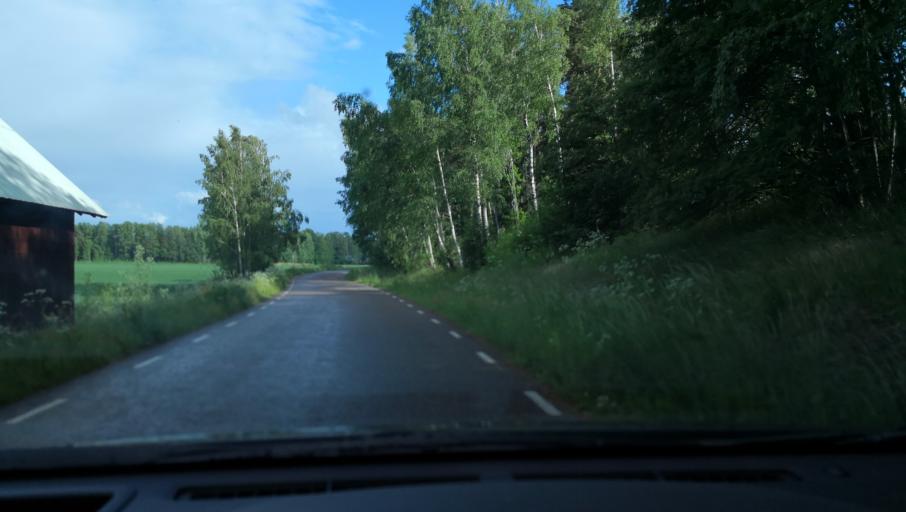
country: SE
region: OErebro
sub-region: Lindesbergs Kommun
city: Fellingsbro
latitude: 59.3094
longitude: 15.6787
